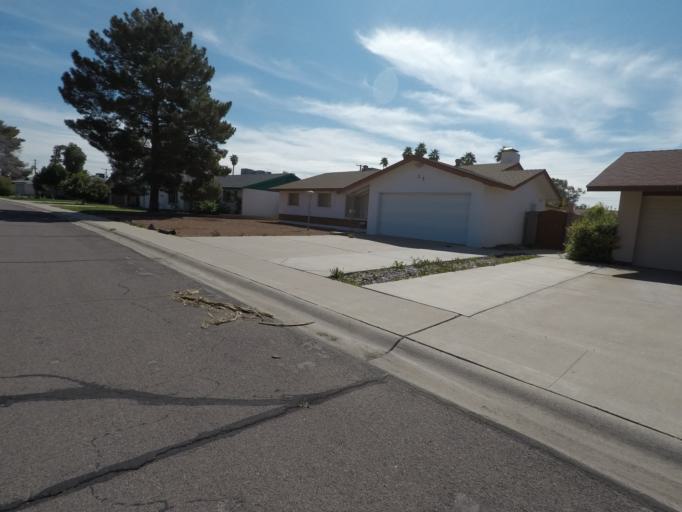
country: US
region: Arizona
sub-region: Maricopa County
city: Tempe Junction
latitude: 33.3965
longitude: -111.9414
